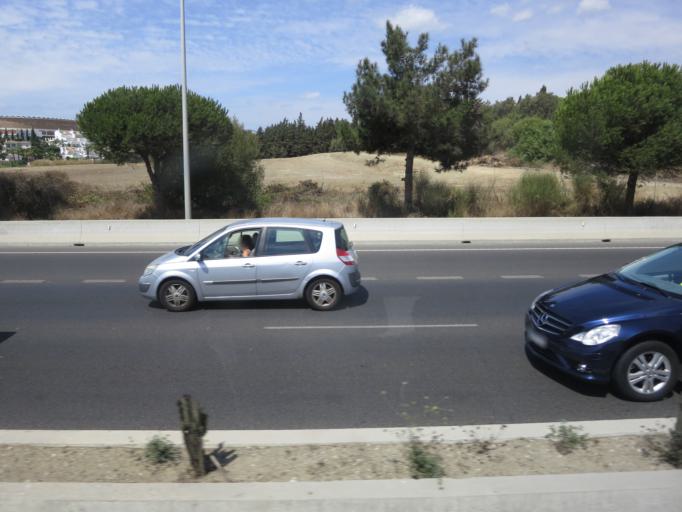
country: ES
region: Andalusia
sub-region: Provincia de Malaga
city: Marbella
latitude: 36.4914
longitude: -4.9538
